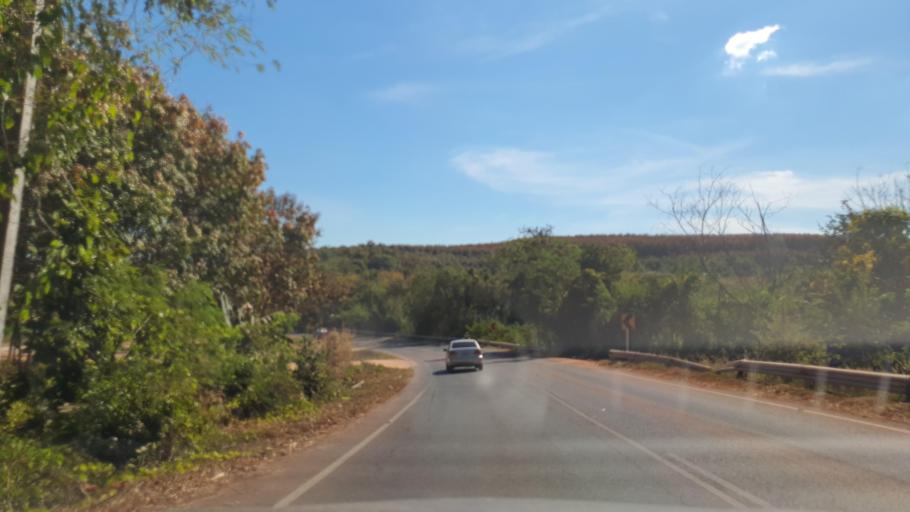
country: TH
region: Kalasin
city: Khao Wong
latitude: 16.7789
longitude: 104.1508
